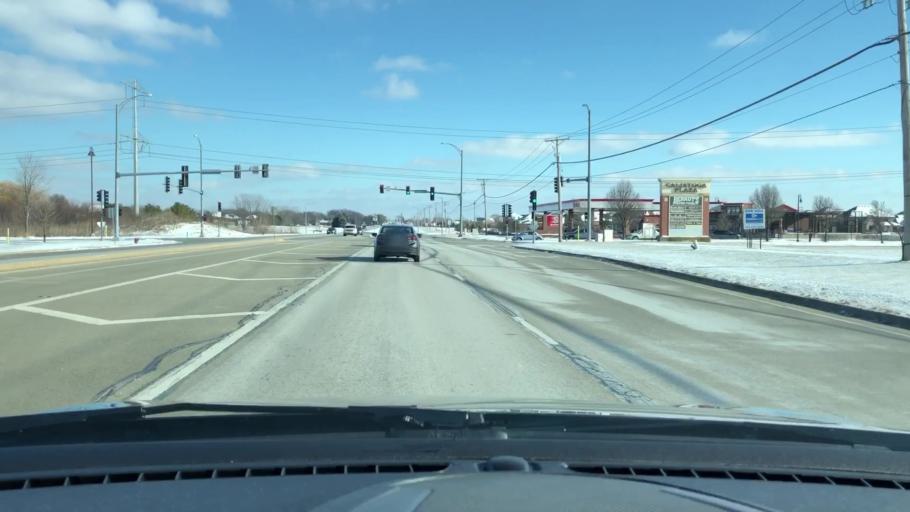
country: US
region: Illinois
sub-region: Will County
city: New Lenox
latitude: 41.4831
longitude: -87.9583
